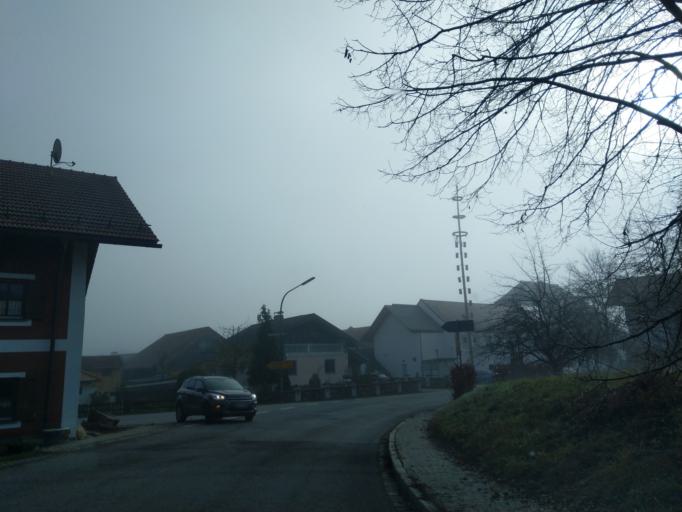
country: DE
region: Bavaria
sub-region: Lower Bavaria
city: Aussernzell
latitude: 48.7250
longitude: 13.2039
